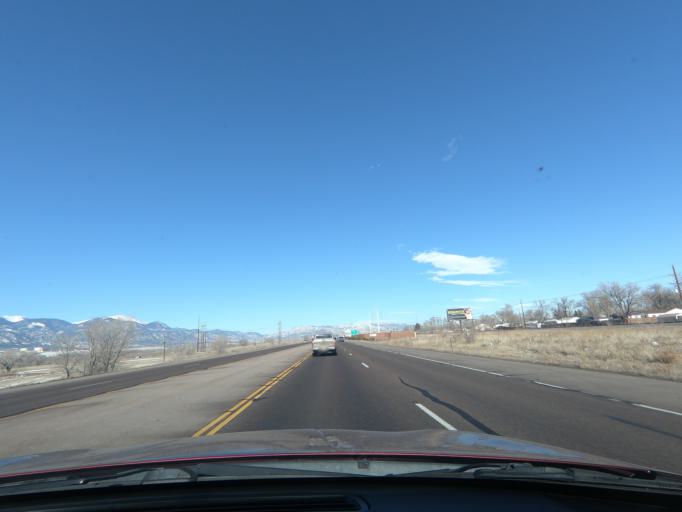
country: US
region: Colorado
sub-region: El Paso County
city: Stratmoor
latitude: 38.7632
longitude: -104.7555
